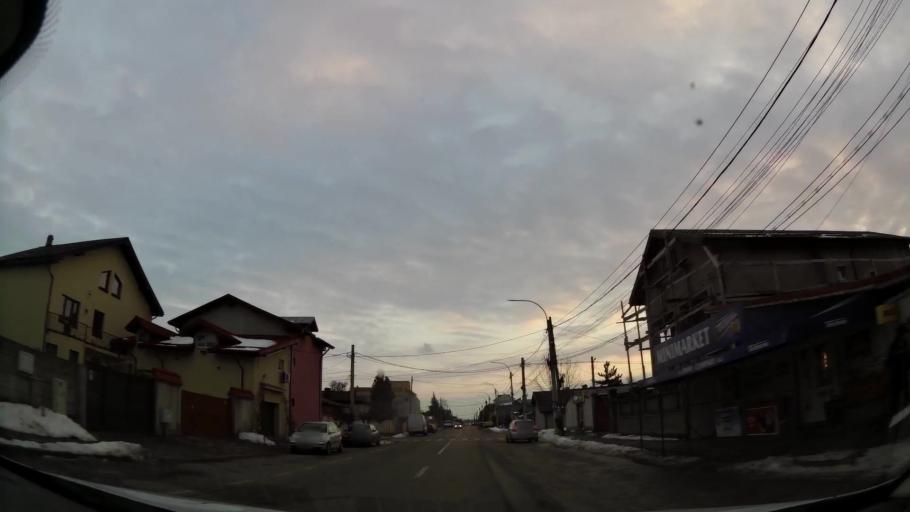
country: RO
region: Ilfov
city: Dobroesti
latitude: 44.4522
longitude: 26.1854
